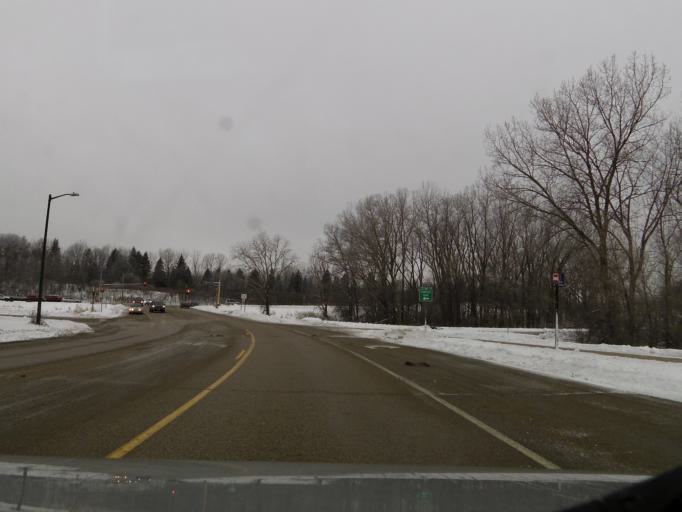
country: US
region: Minnesota
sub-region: Dakota County
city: West Saint Paul
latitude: 44.8834
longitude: -93.0897
